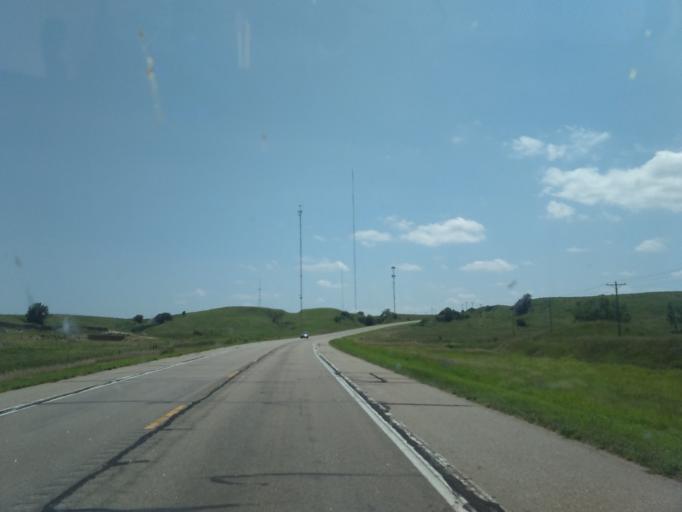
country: US
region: Nebraska
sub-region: Dawson County
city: Lexington
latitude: 40.7070
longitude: -99.7873
